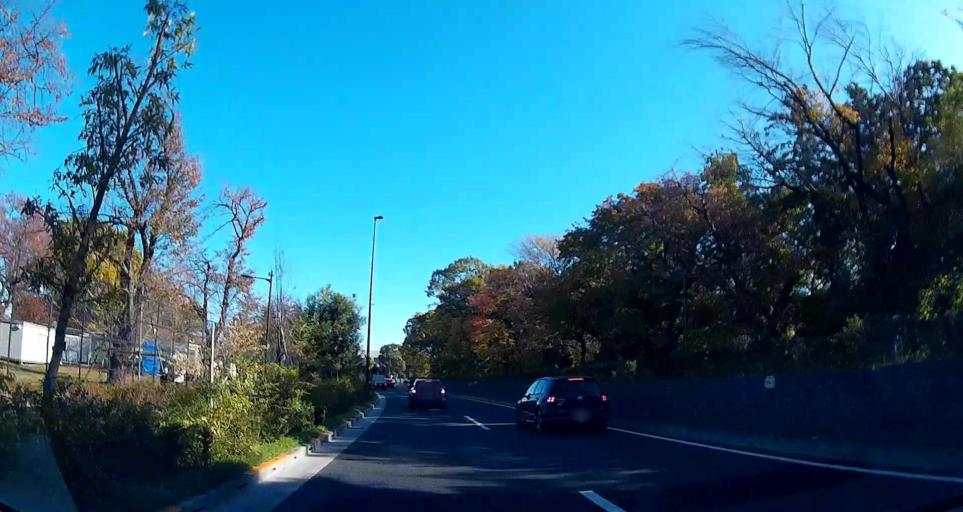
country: JP
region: Tokyo
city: Mitaka-shi
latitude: 35.6815
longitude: 139.6029
